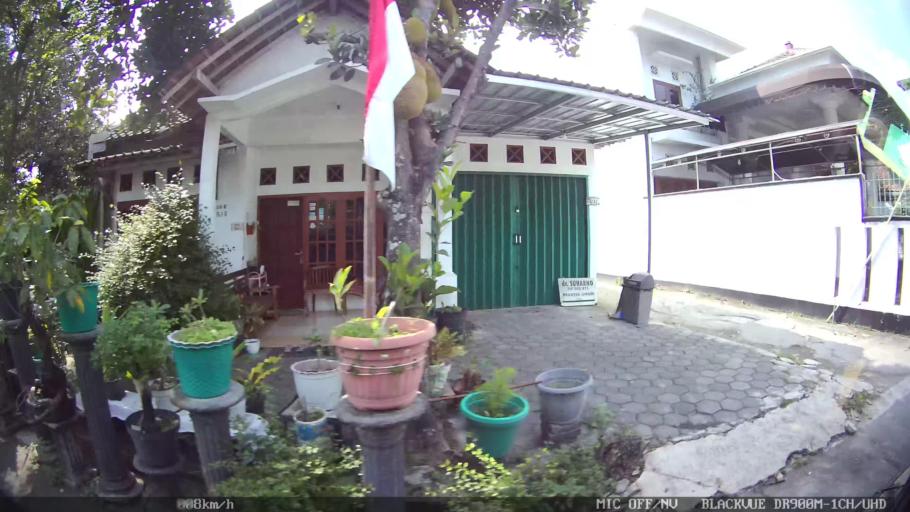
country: ID
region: Daerah Istimewa Yogyakarta
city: Yogyakarta
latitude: -7.8066
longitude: 110.3805
